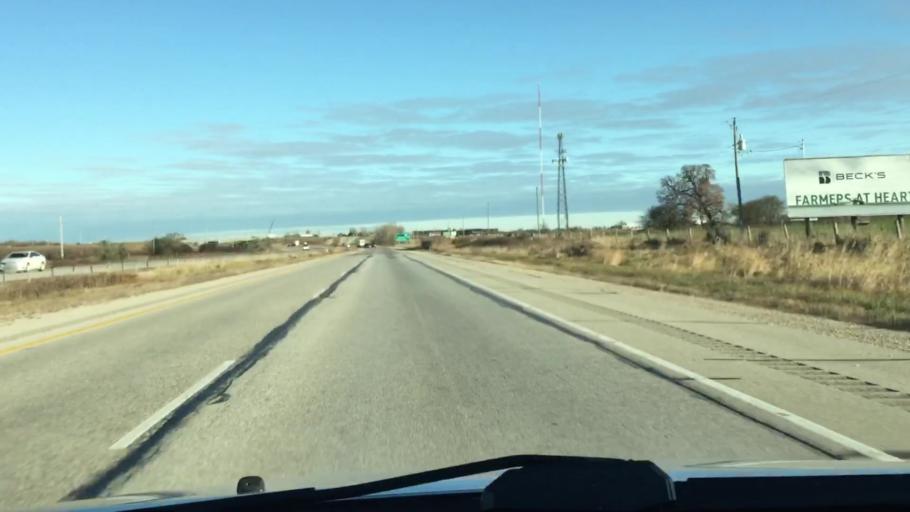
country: US
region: Wisconsin
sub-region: Fond du Lac County
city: Fond du Lac
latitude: 43.7283
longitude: -88.4421
